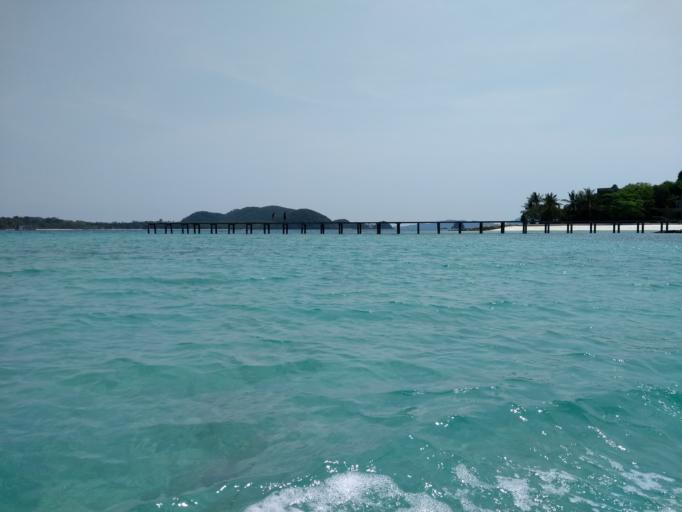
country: TH
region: Trat
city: Ko Chang Tai
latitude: 11.8329
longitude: 102.4621
